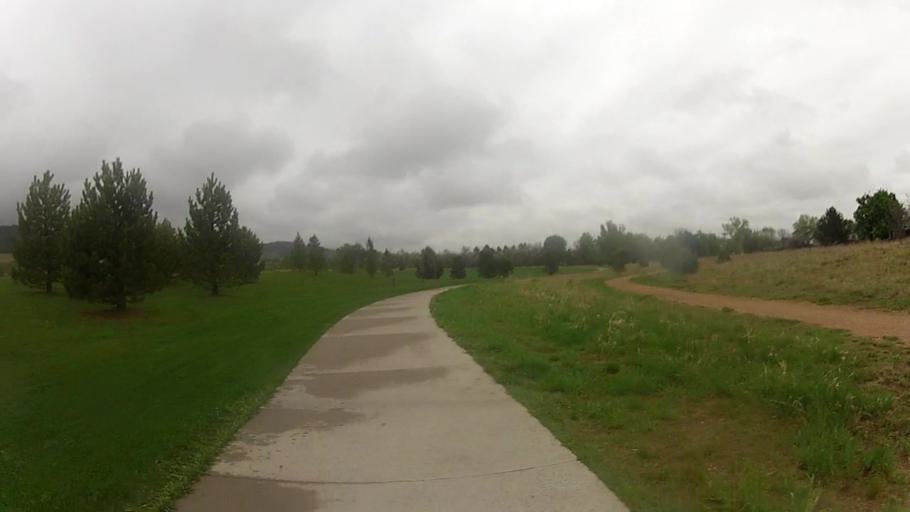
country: US
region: Colorado
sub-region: Larimer County
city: Fort Collins
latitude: 40.5401
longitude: -105.1228
